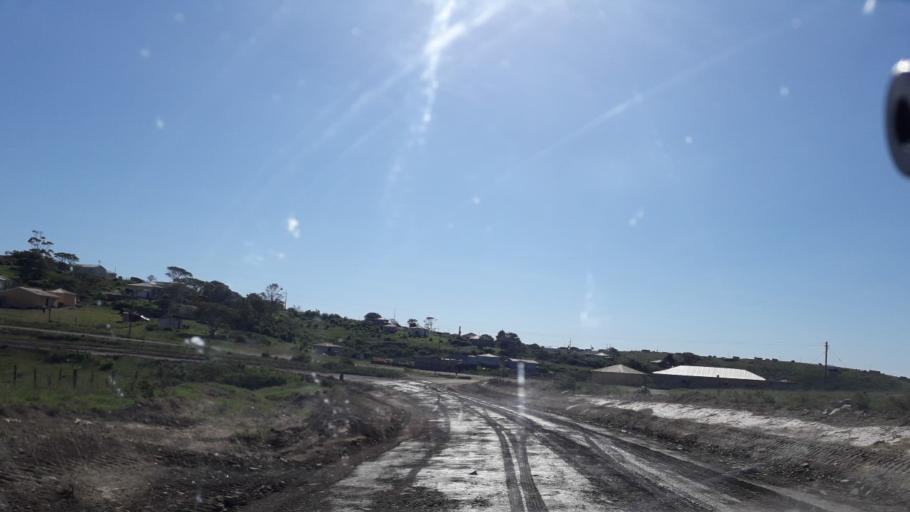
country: ZA
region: Eastern Cape
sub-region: Buffalo City Metropolitan Municipality
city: East London
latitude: -32.8262
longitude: 27.9730
